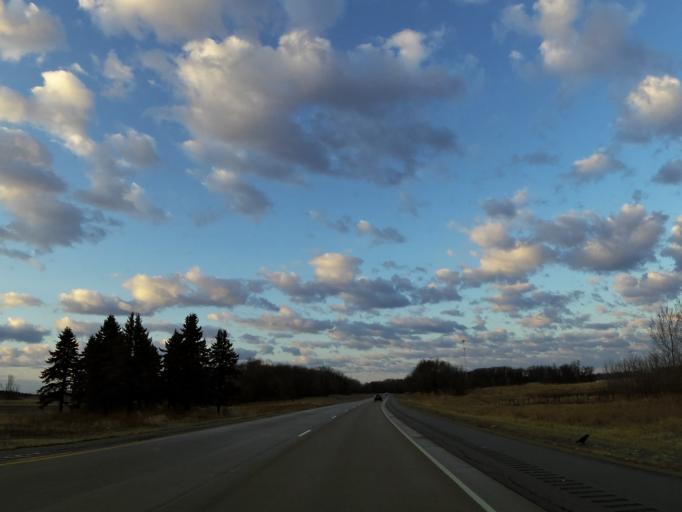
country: US
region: Minnesota
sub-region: Rice County
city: Faribault
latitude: 44.3859
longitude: -93.2931
